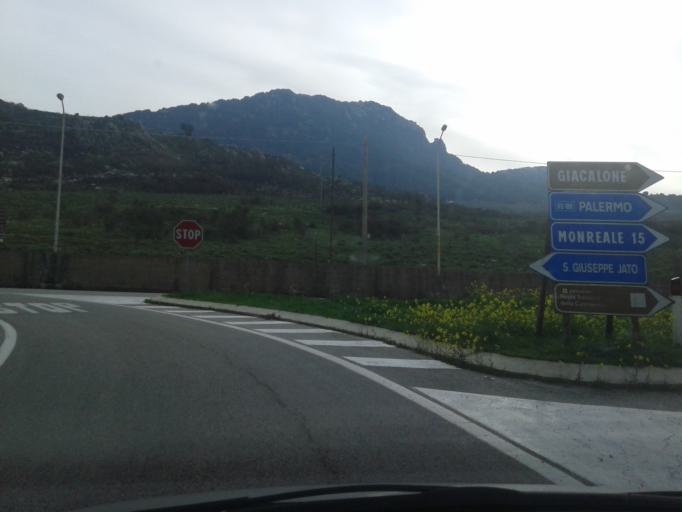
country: IT
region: Sicily
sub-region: Palermo
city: Giacalone
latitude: 38.0275
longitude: 13.2414
